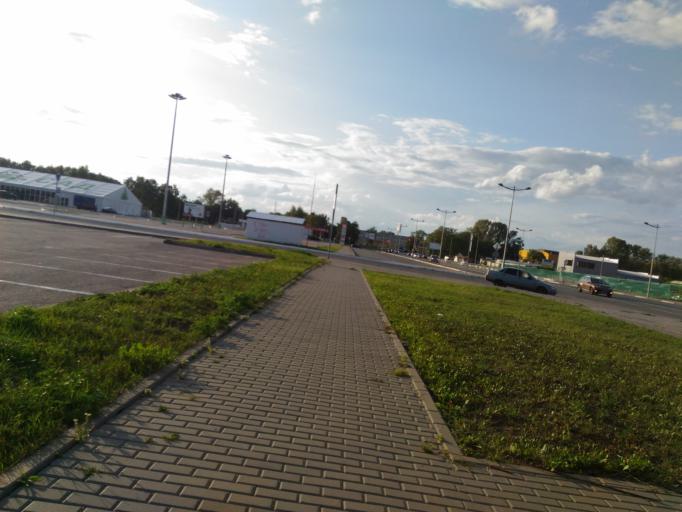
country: RU
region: Ulyanovsk
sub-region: Ulyanovskiy Rayon
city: Ulyanovsk
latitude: 54.2907
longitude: 48.2719
